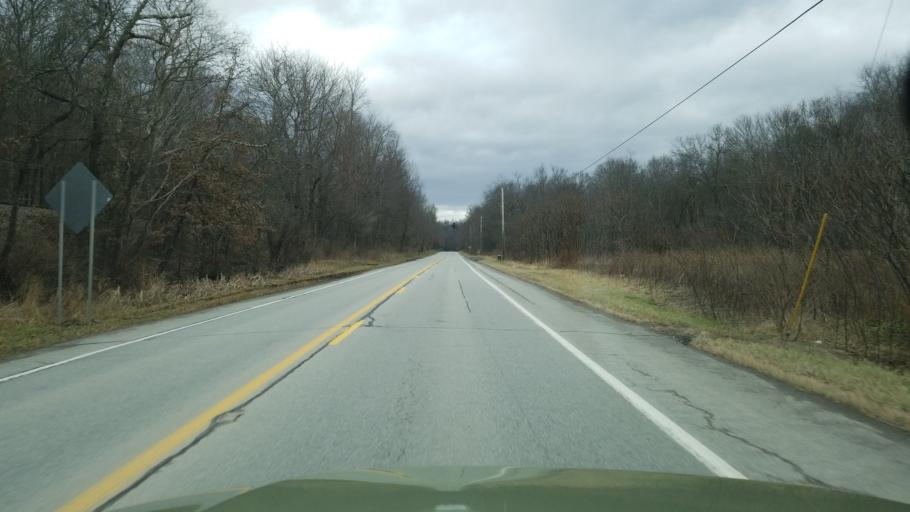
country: US
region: Pennsylvania
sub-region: Indiana County
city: Clymer
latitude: 40.7803
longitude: -79.0539
